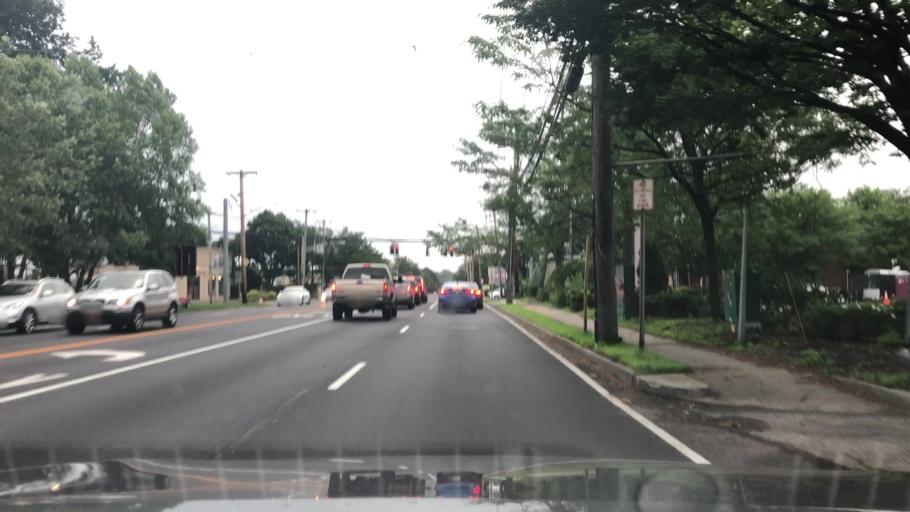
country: US
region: New York
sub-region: Nassau County
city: Woodbury
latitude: 40.8141
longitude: -73.4782
